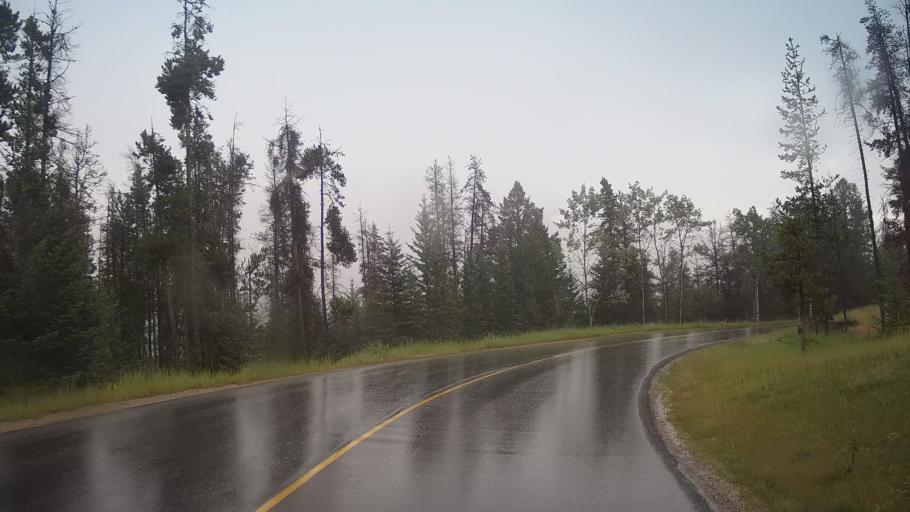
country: CA
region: Alberta
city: Jasper Park Lodge
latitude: 52.8911
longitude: -118.0819
